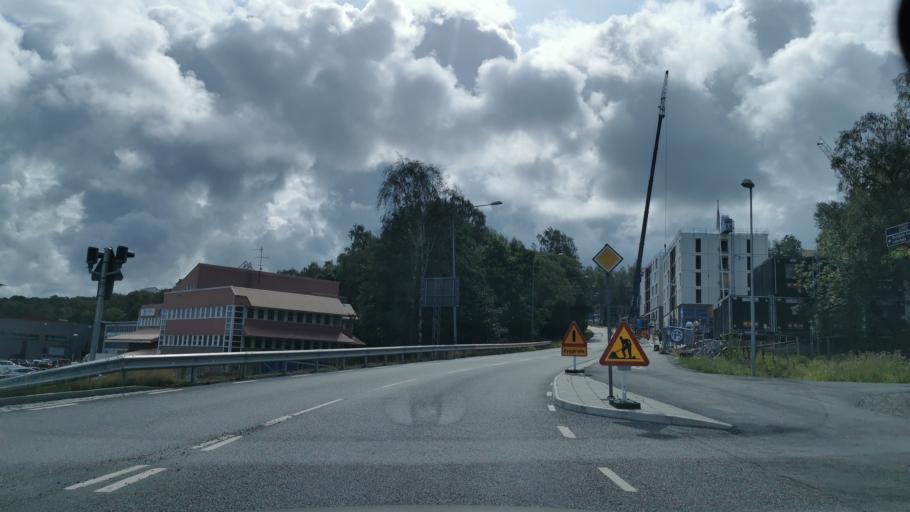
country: SE
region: Vaestra Goetaland
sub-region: Goteborg
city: Majorna
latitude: 57.6387
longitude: 11.9517
